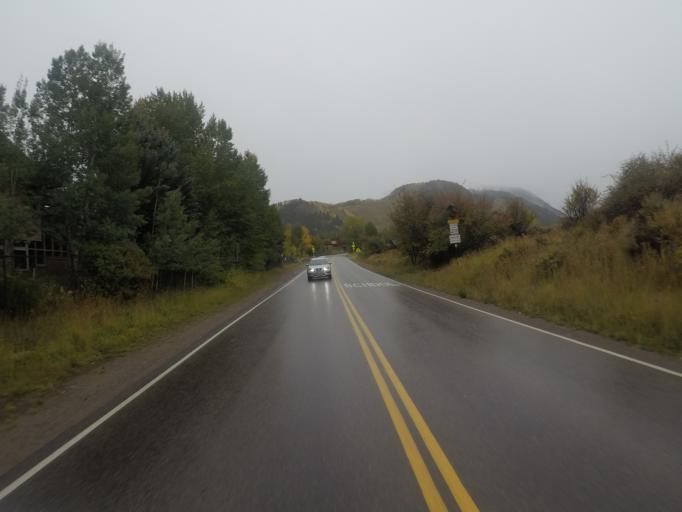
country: US
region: Colorado
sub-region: Pitkin County
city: Aspen
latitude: 39.1911
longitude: -106.8501
